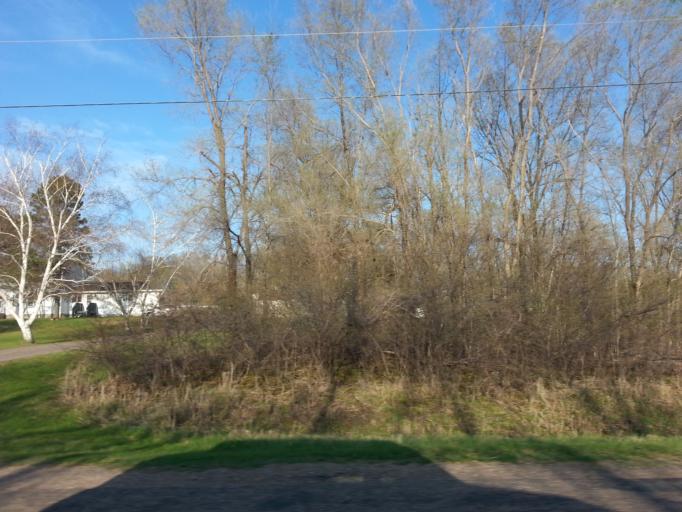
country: US
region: Wisconsin
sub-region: Pierce County
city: River Falls
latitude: 44.8898
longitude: -92.6496
